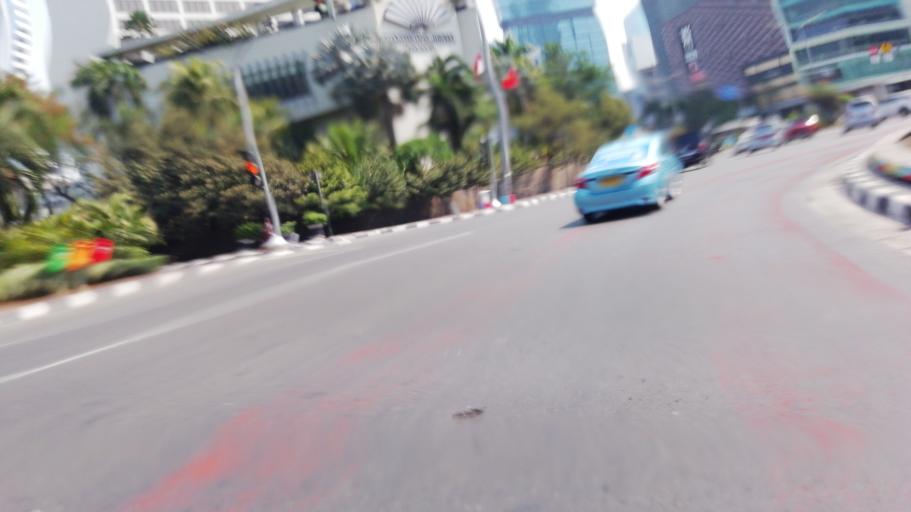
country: ID
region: Jakarta Raya
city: Jakarta
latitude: -6.1951
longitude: 106.8235
